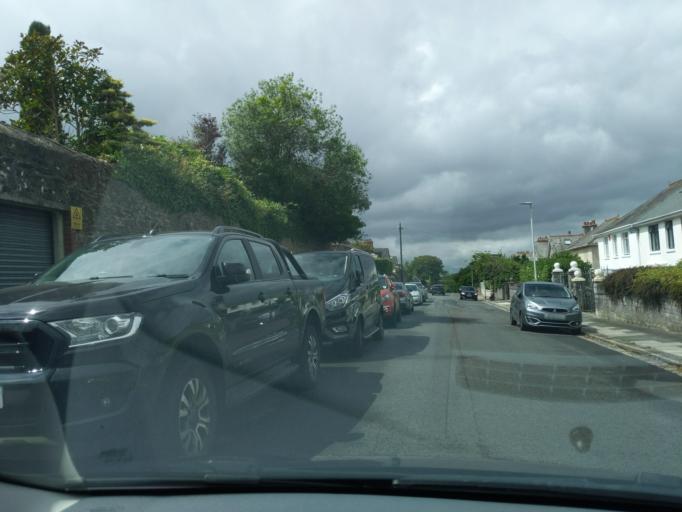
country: GB
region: England
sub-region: Plymouth
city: Plymouth
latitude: 50.3875
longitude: -4.1262
